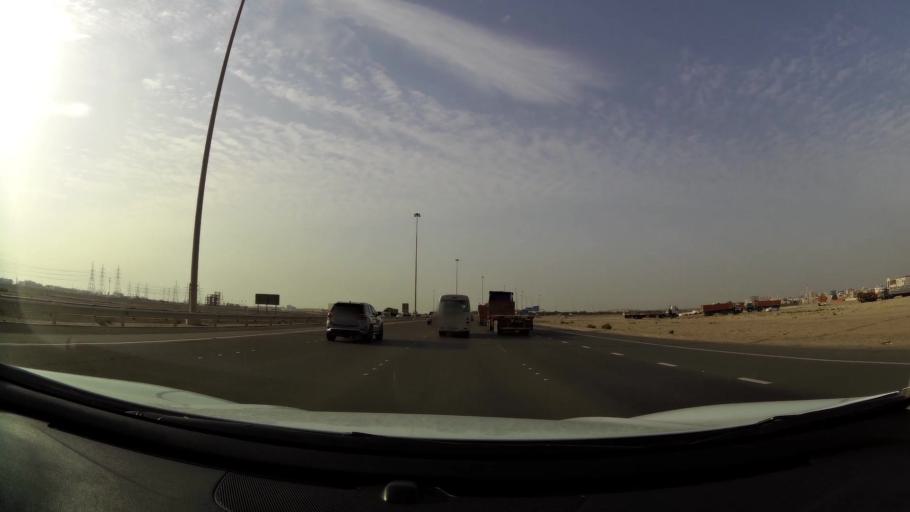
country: AE
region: Abu Dhabi
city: Abu Dhabi
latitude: 24.3086
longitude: 54.5292
